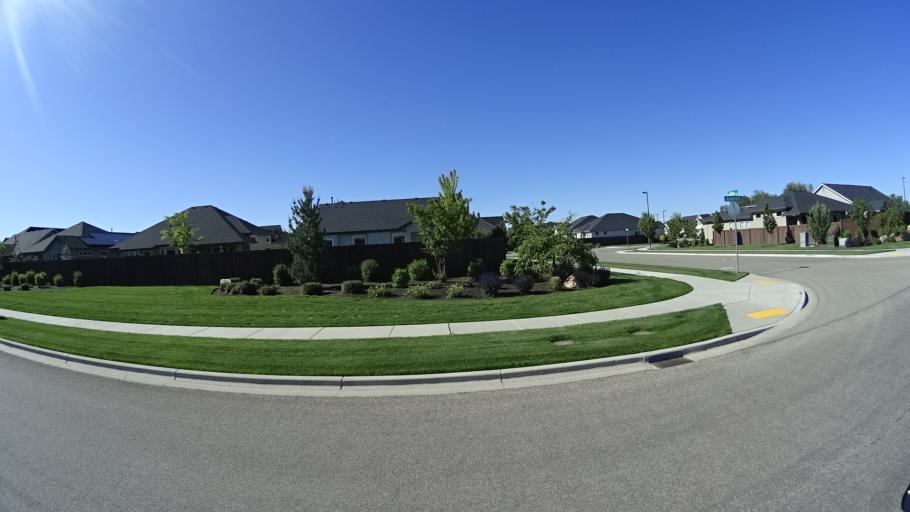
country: US
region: Idaho
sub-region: Ada County
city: Star
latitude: 43.6580
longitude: -116.4518
